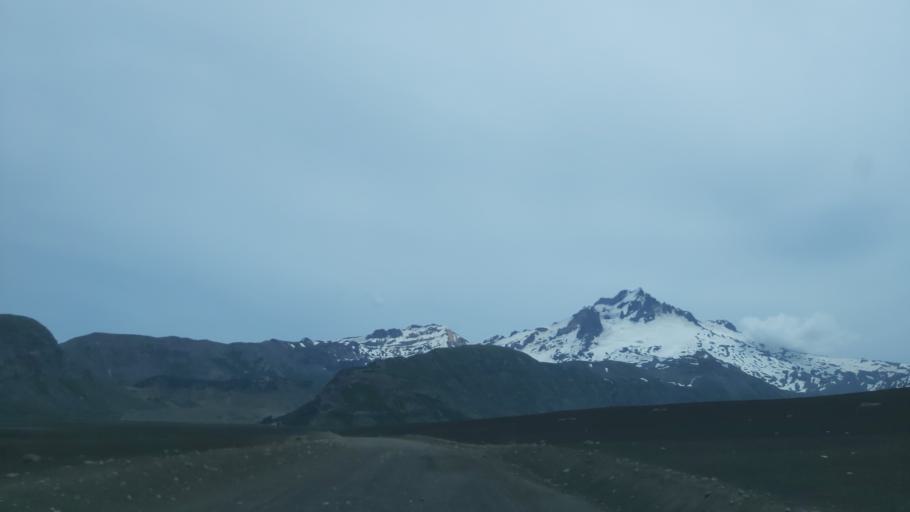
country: AR
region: Neuquen
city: Andacollo
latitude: -37.4572
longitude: -71.2978
